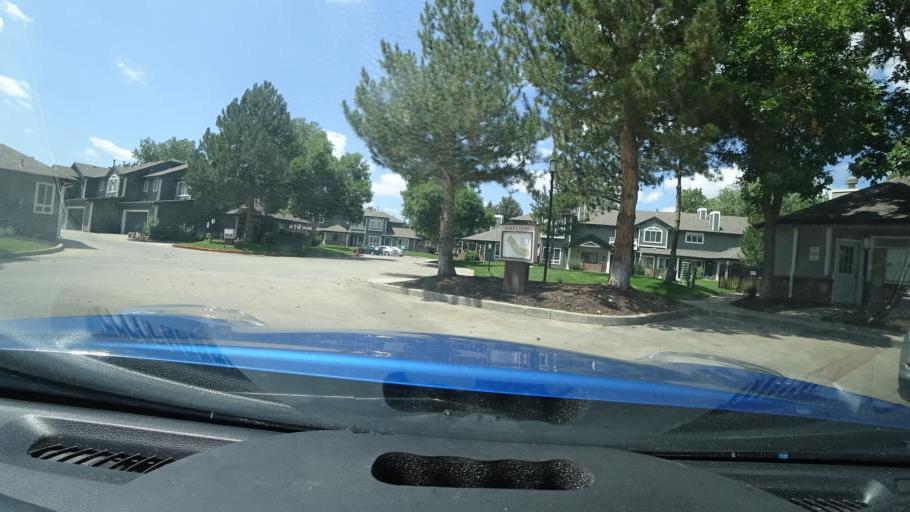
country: US
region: Colorado
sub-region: Arapahoe County
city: Glendale
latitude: 39.6990
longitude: -104.8854
